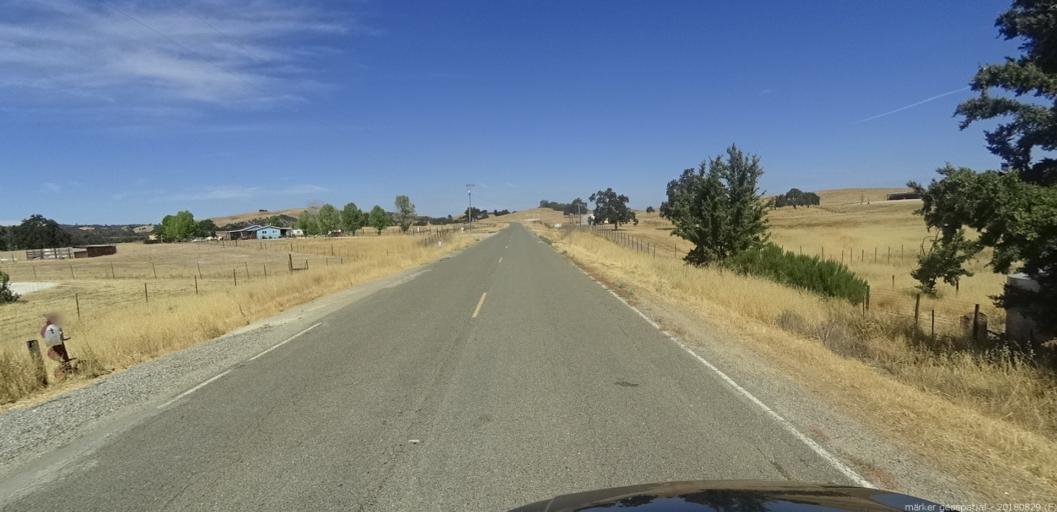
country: US
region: California
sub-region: San Luis Obispo County
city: Lake Nacimiento
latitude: 35.8335
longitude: -121.0272
